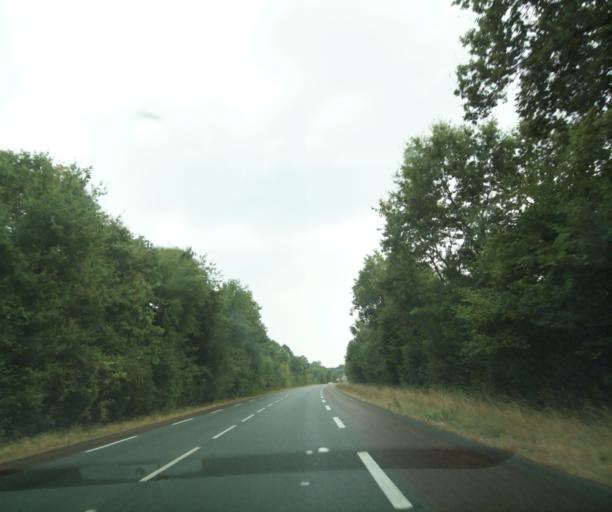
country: FR
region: Poitou-Charentes
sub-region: Departement de la Charente-Maritime
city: Cabariot
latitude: 45.9468
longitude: -0.8660
